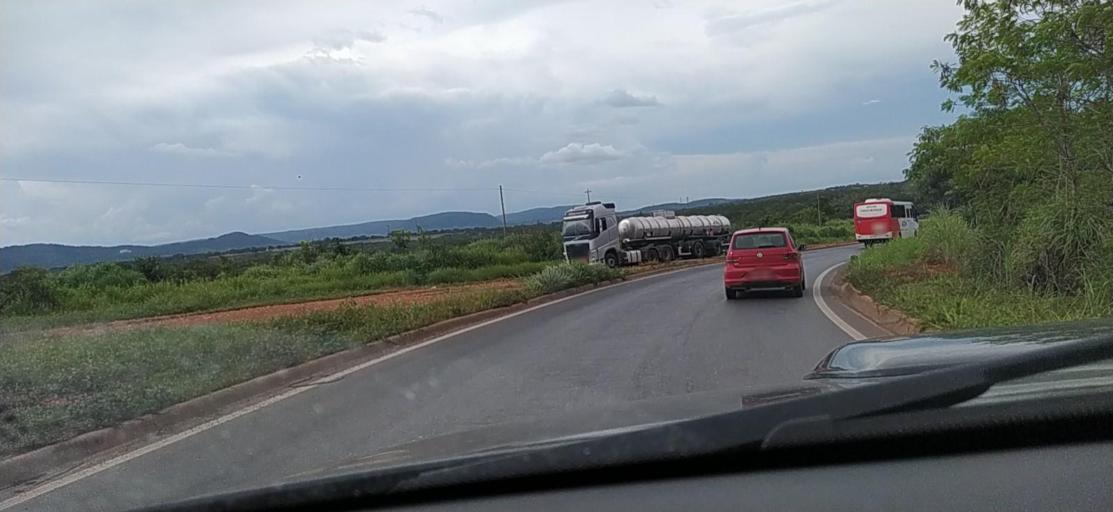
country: BR
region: Minas Gerais
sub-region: Montes Claros
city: Montes Claros
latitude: -16.6767
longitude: -43.7993
